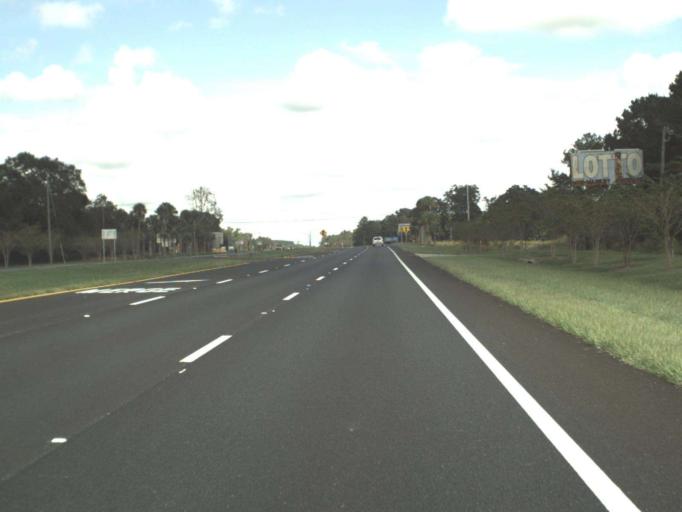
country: US
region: Florida
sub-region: Jackson County
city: Graceville
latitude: 30.9952
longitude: -85.4077
